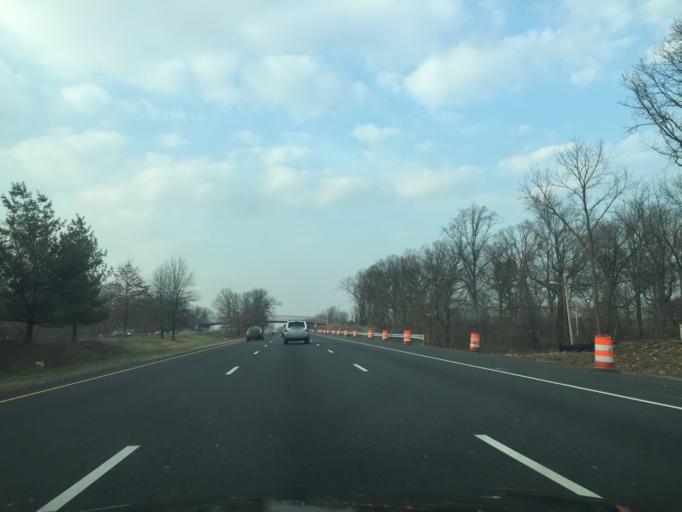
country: US
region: Maryland
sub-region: Baltimore County
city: Baltimore Highlands
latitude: 39.2356
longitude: -76.6492
